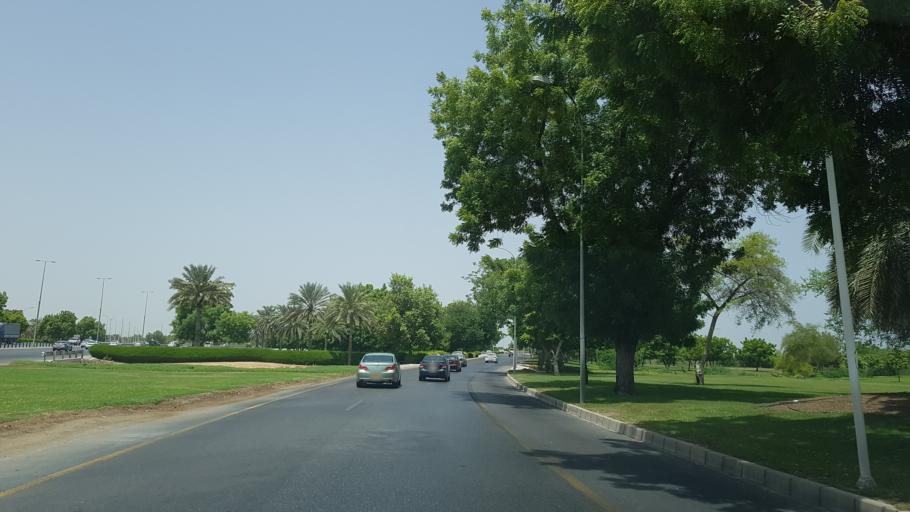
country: OM
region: Muhafazat Masqat
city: As Sib al Jadidah
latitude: 23.5848
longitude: 58.2599
